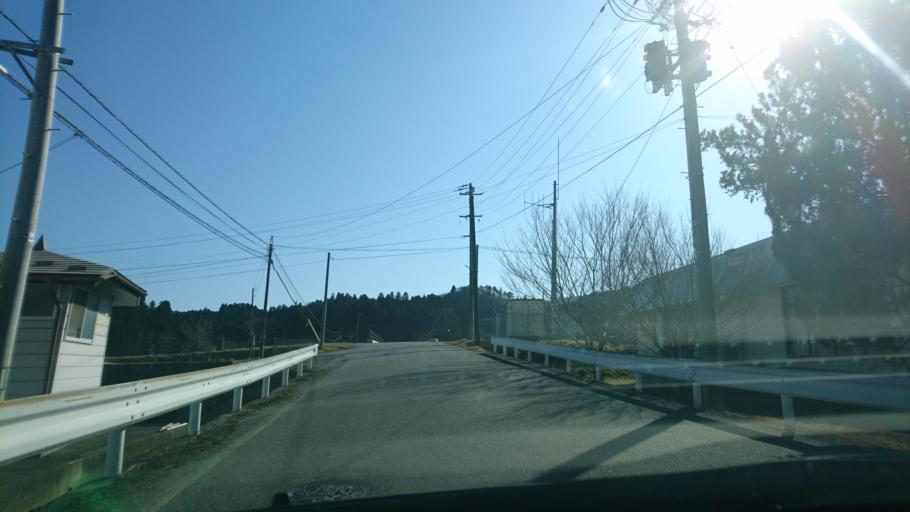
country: JP
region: Iwate
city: Ichinoseki
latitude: 38.8485
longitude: 141.2948
